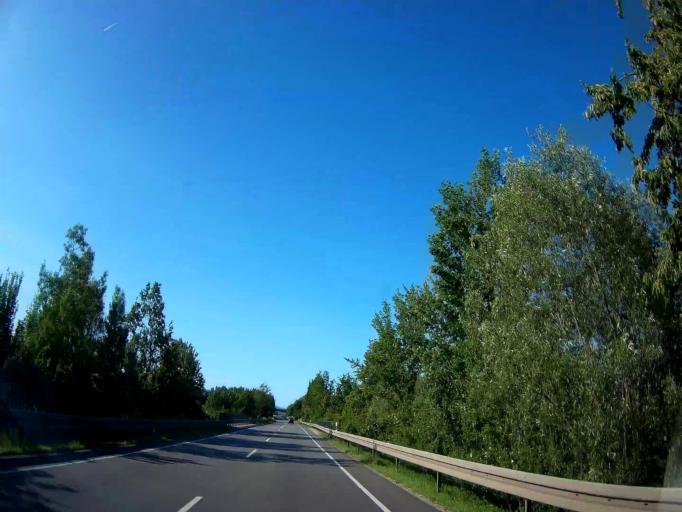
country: DE
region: Bavaria
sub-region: Lower Bavaria
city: Oberschneiding
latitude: 48.7995
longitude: 12.6532
